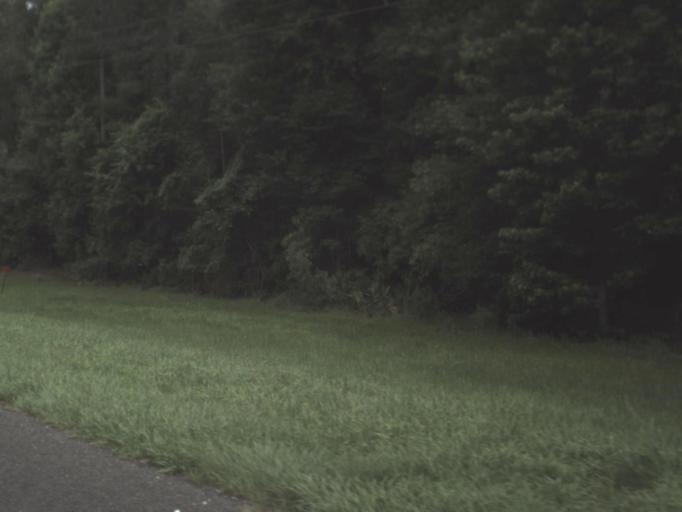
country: US
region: Georgia
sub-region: Charlton County
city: Folkston
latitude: 30.7637
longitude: -81.9683
